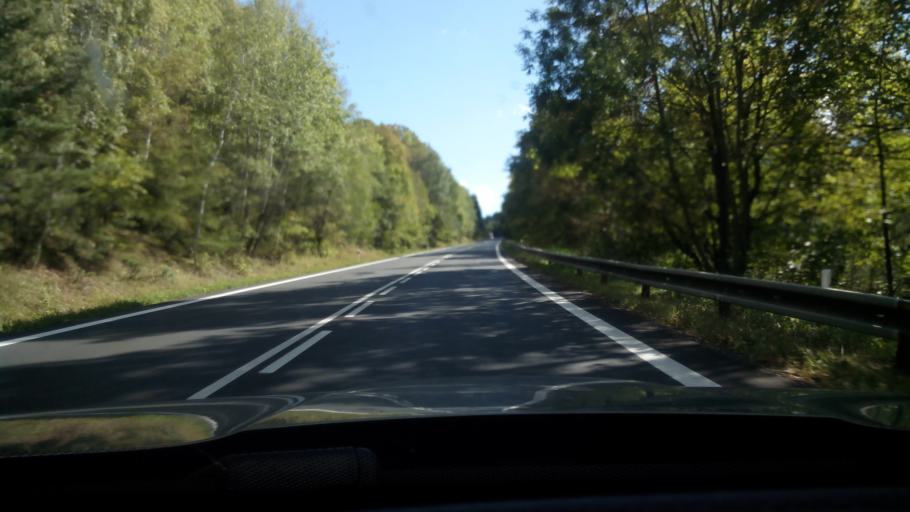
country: CZ
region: Jihocesky
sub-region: Okres Prachatice
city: Zdikov
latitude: 49.0727
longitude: 13.7122
